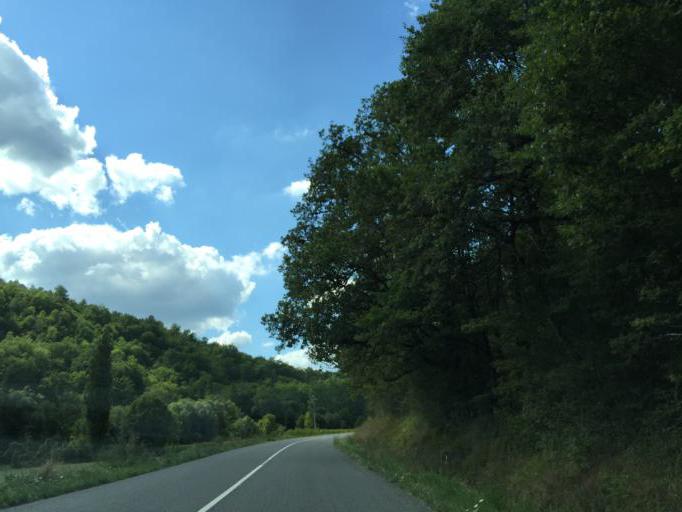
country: FR
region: Midi-Pyrenees
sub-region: Departement de l'Aveyron
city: Saint-Christophe-Vallon
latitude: 44.5245
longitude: 2.4154
